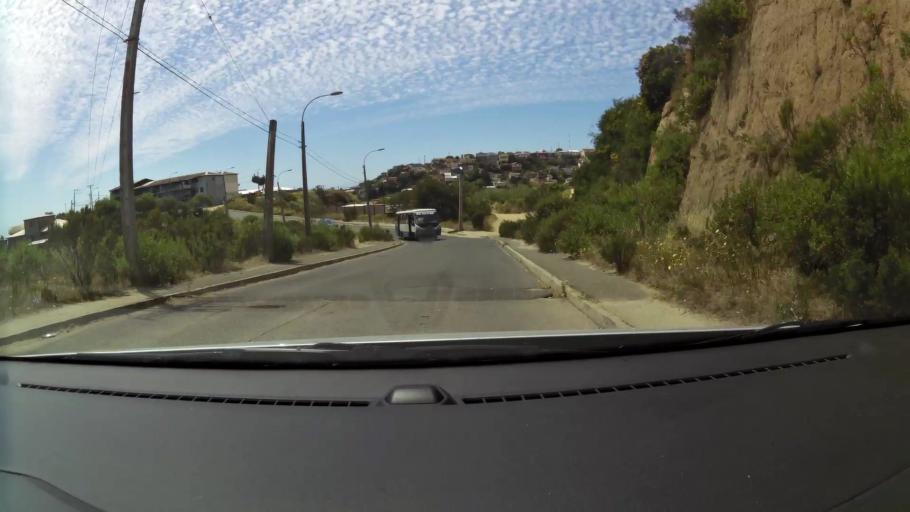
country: CL
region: Valparaiso
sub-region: Provincia de Valparaiso
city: Vina del Mar
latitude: -33.0574
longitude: -71.5679
